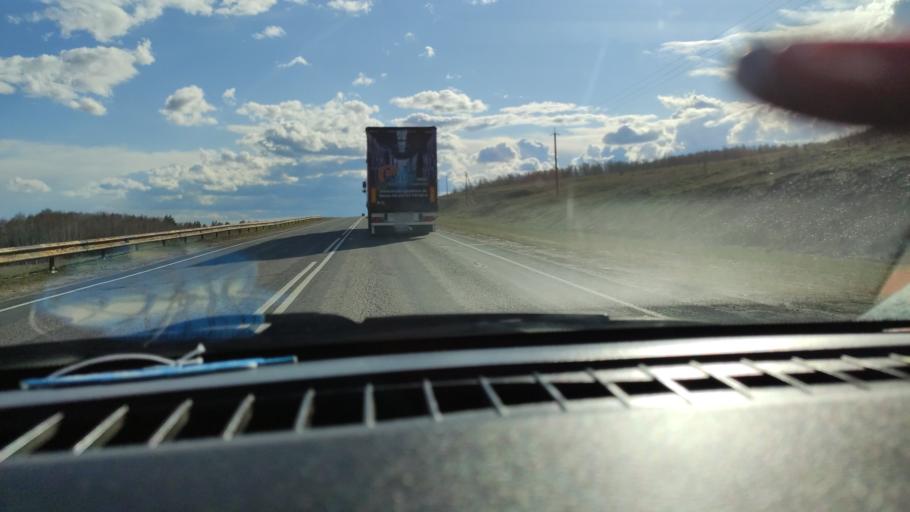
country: RU
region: Saratov
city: Sinodskoye
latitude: 52.0715
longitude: 46.7788
